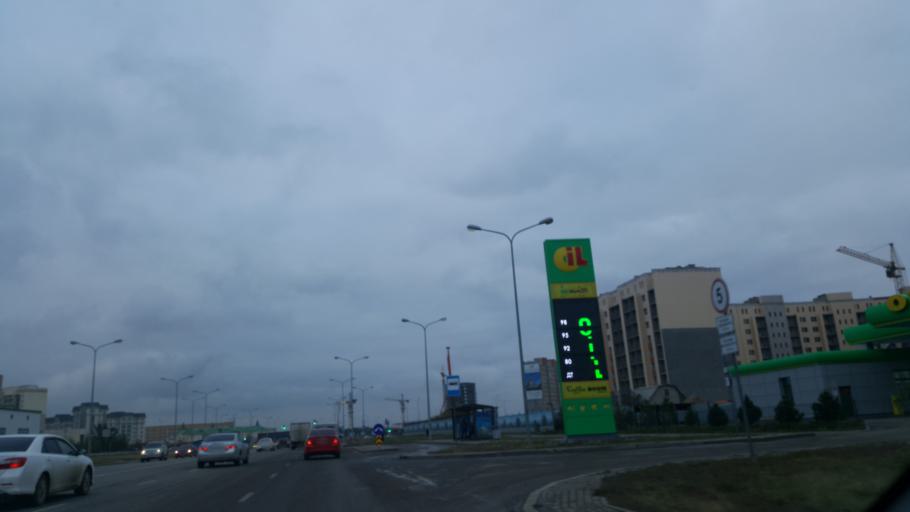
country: KZ
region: Astana Qalasy
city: Astana
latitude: 51.1281
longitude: 71.4851
